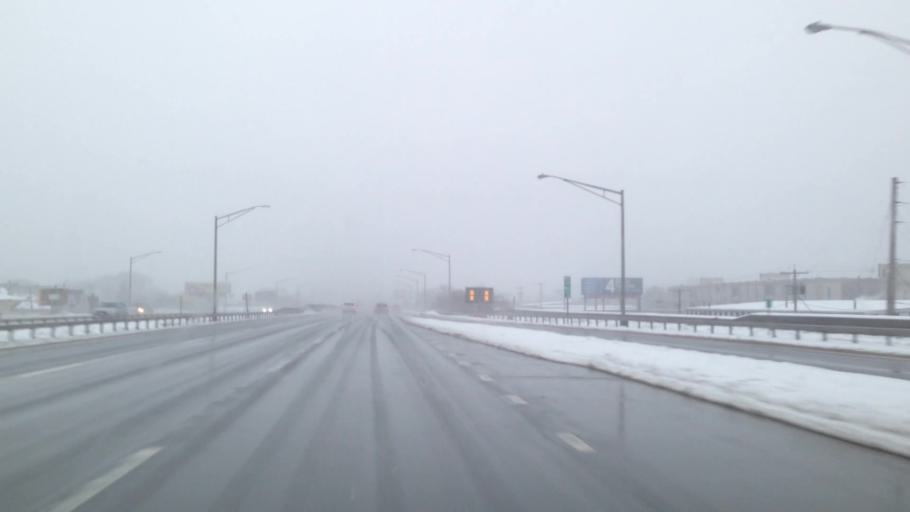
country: US
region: New York
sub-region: Onondaga County
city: Syracuse
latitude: 43.0514
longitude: -76.1384
